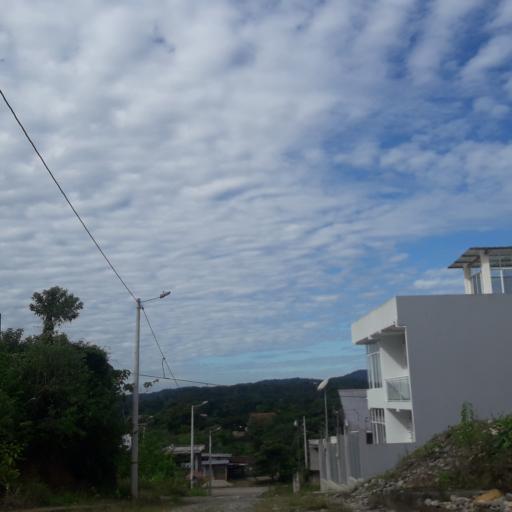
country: EC
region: Napo
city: Tena
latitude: -0.9820
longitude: -77.8259
